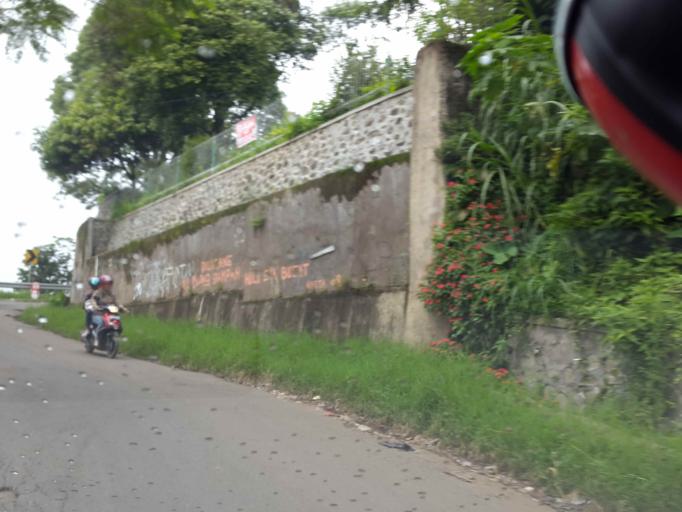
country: ID
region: West Java
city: Lembang
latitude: -6.8221
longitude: 107.5751
